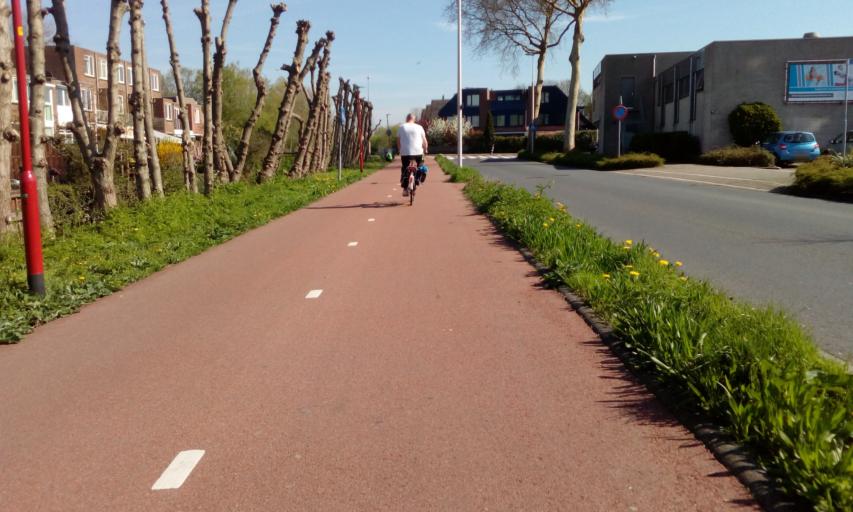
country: NL
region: South Holland
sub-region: Gemeente Zoetermeer
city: Zoetermeer
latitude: 52.0640
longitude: 4.5123
